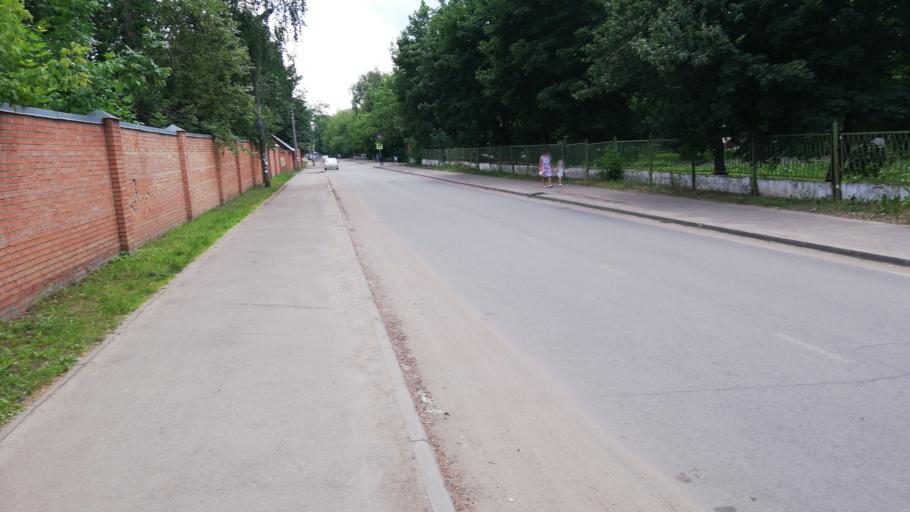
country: RU
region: Jaroslavl
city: Yaroslavl
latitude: 57.6396
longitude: 39.8658
